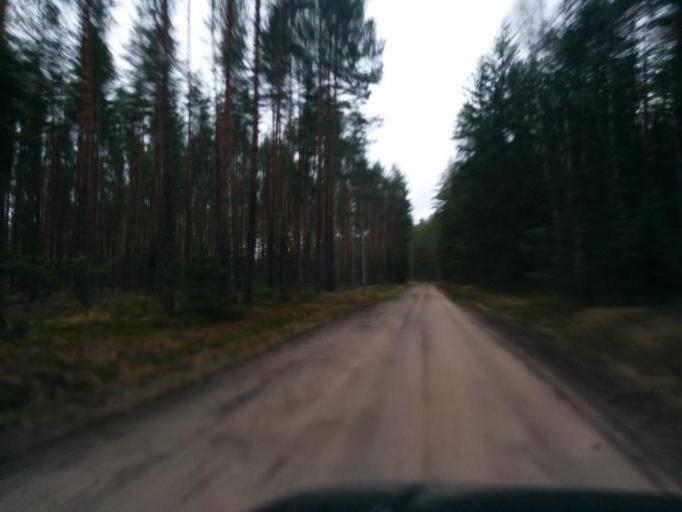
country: LV
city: Tireli
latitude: 56.7997
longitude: 23.6756
